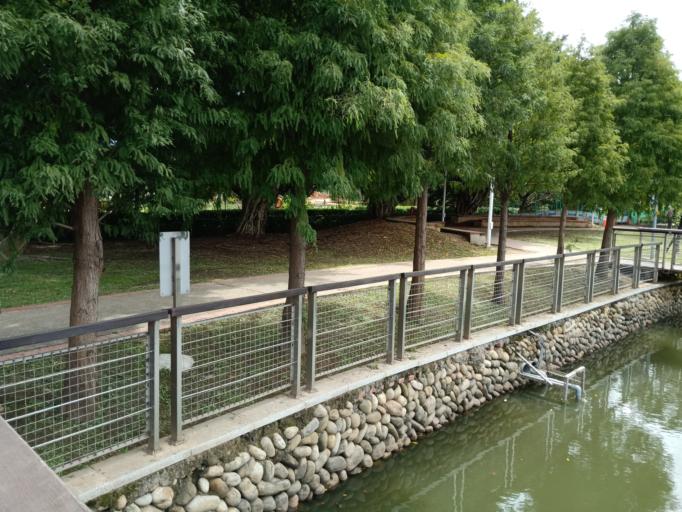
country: TW
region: Taiwan
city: Taoyuan City
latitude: 24.9413
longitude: 121.2585
